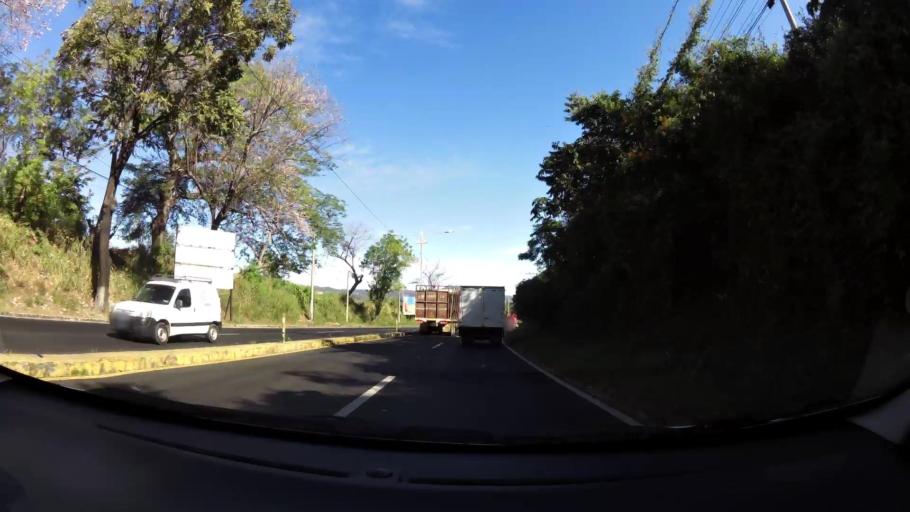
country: SV
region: Santa Ana
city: Santa Ana
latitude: 13.9601
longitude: -89.5692
